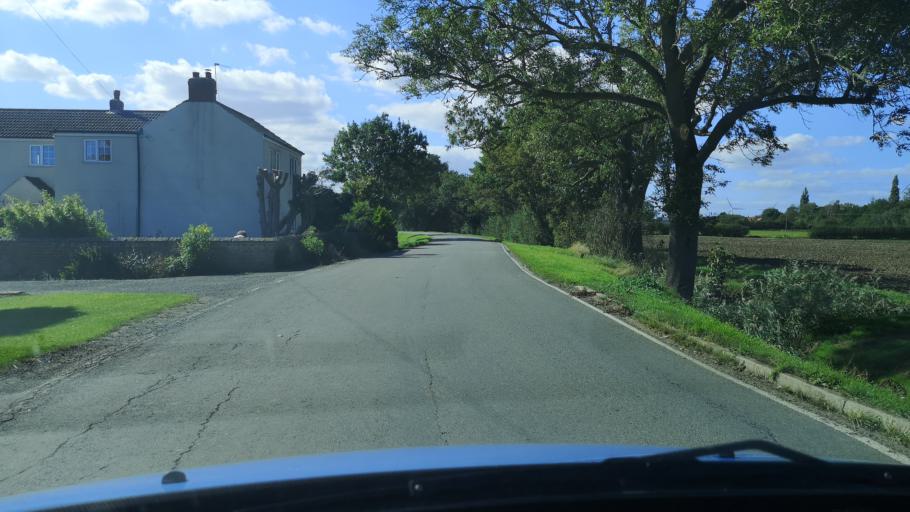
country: GB
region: England
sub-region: North Lincolnshire
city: Eastoft
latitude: 53.6360
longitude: -0.7735
